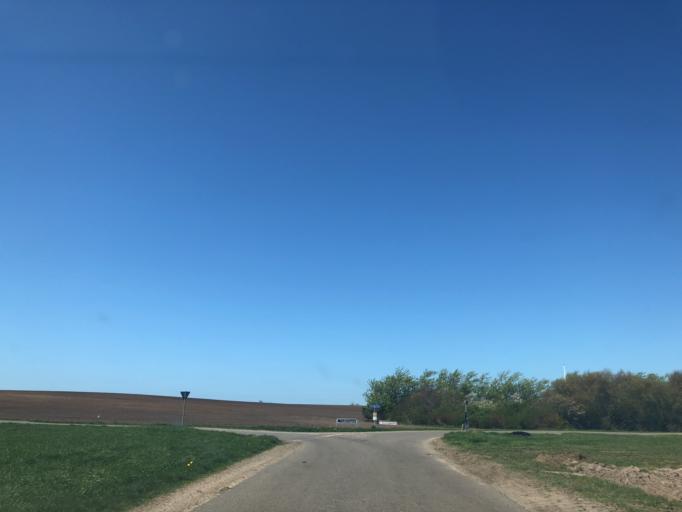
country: DK
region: Central Jutland
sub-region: Holstebro Kommune
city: Vinderup
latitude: 56.5272
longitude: 8.7756
